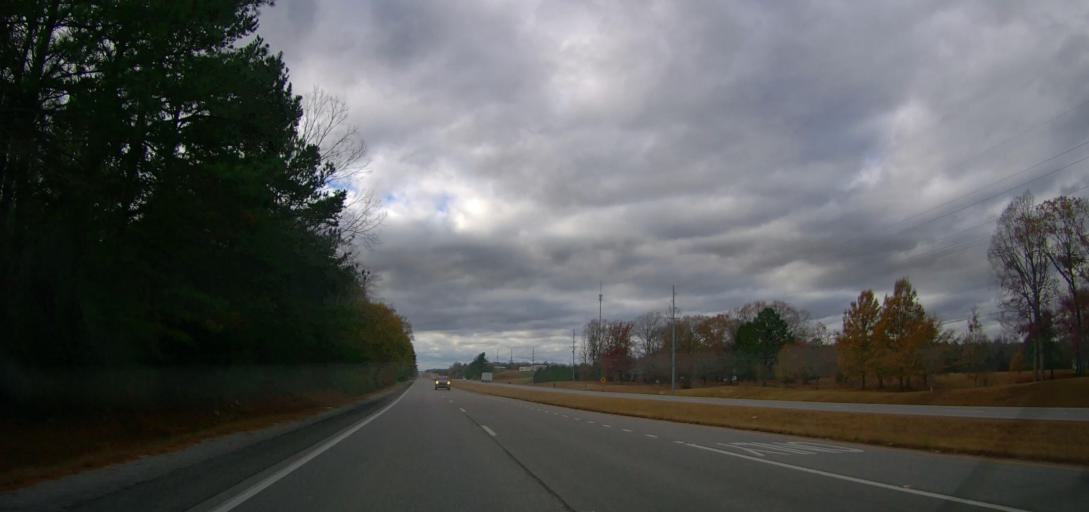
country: US
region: Alabama
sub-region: Lawrence County
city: Moulton
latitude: 34.5539
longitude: -87.3217
